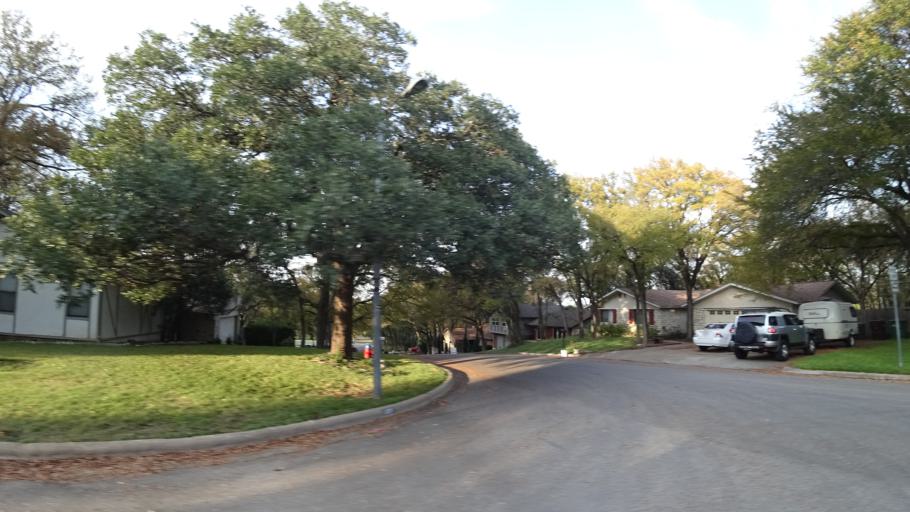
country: US
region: Texas
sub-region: Williamson County
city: Round Rock
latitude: 30.5068
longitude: -97.6701
